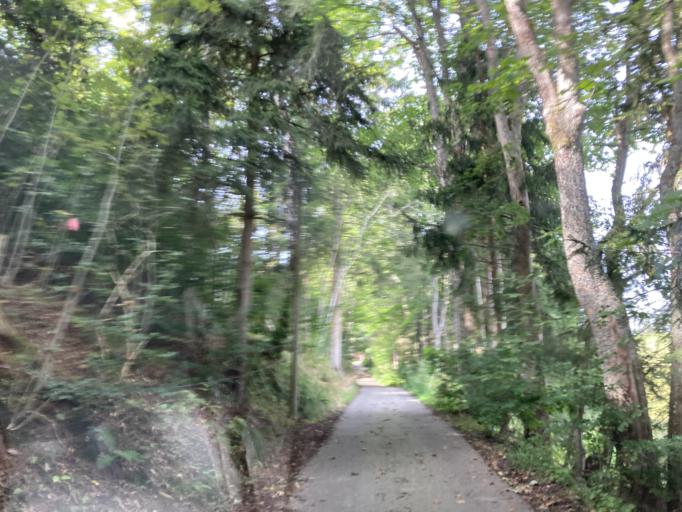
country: DE
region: Baden-Wuerttemberg
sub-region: Freiburg Region
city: Sankt Georgen im Schwarzwald
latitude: 48.1184
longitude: 8.3141
